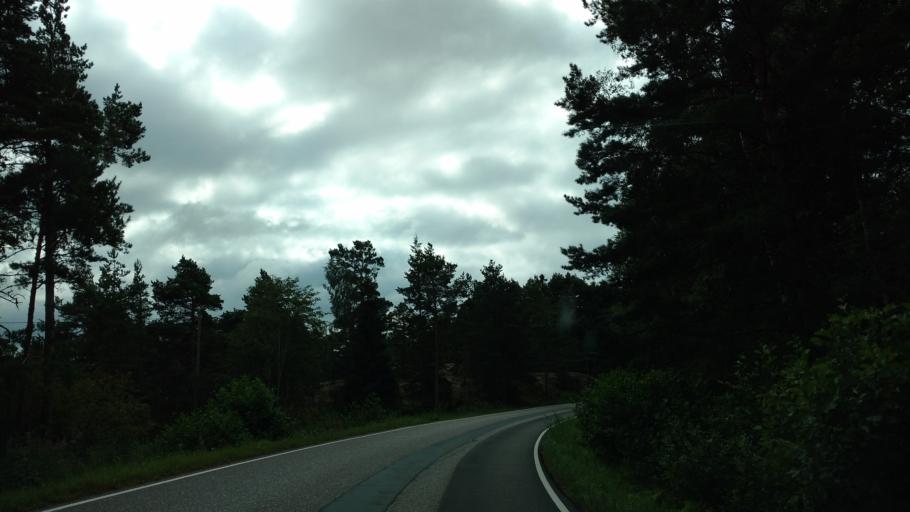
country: FI
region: Varsinais-Suomi
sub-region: Aboland-Turunmaa
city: Dragsfjaerd
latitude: 59.9954
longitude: 22.4537
